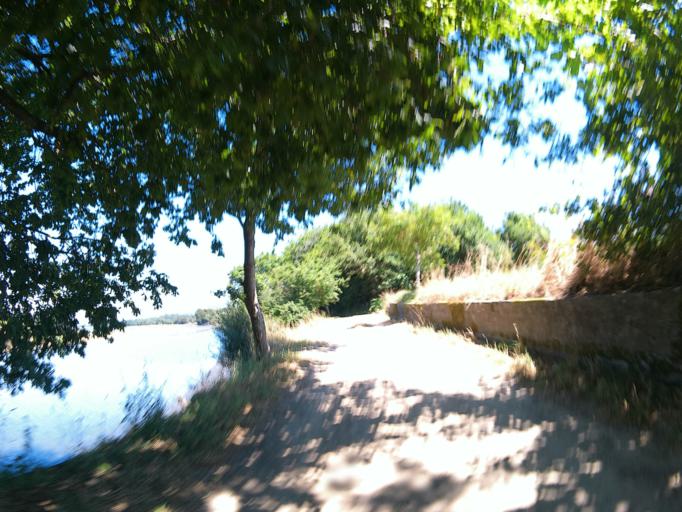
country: PT
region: Viana do Castelo
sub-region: Viana do Castelo
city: Darque
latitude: 41.7001
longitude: -8.7389
